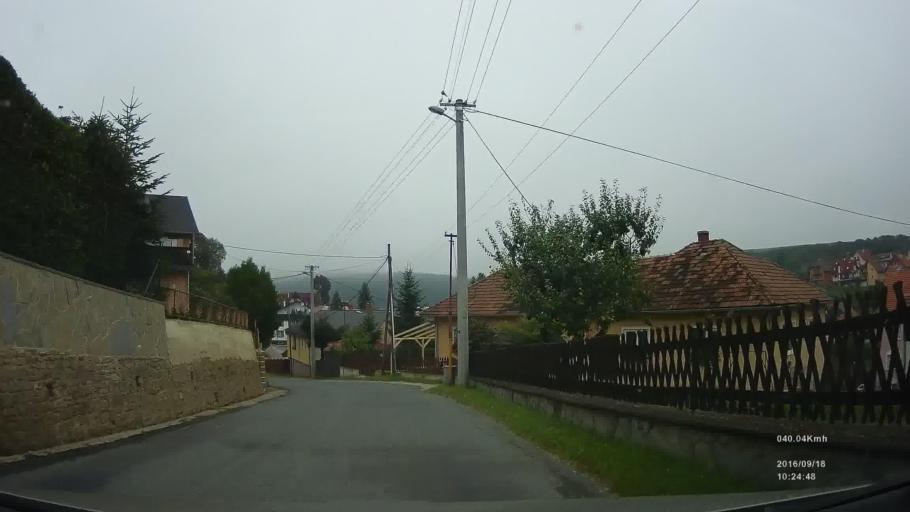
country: SK
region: Kosicky
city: Spisska Nova Ves
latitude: 48.9475
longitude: 20.6183
